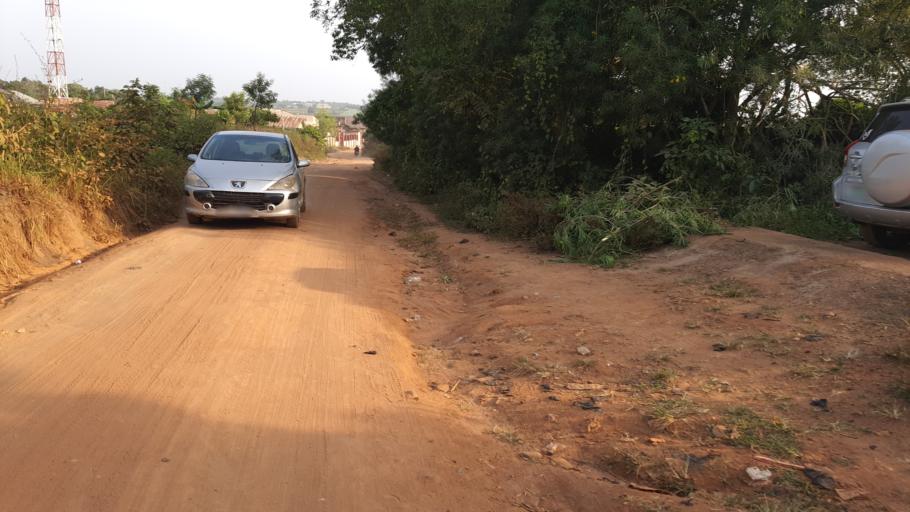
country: NG
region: Osun
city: Iwo
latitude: 7.6253
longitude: 4.1577
